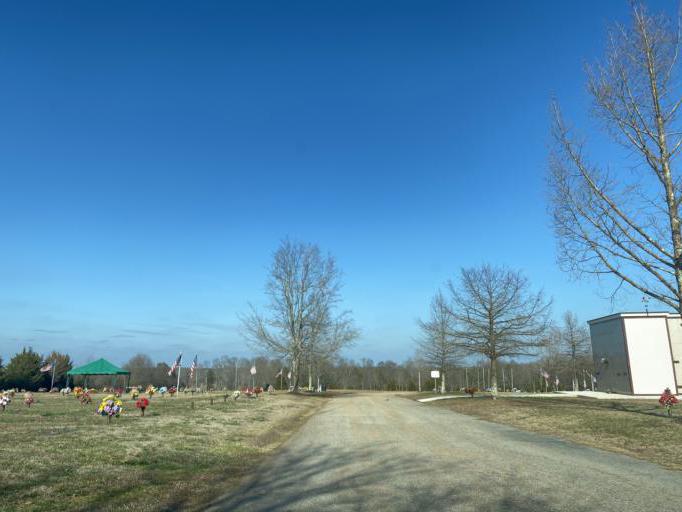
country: US
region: South Carolina
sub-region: Cherokee County
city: Gaffney
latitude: 35.1077
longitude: -81.6957
